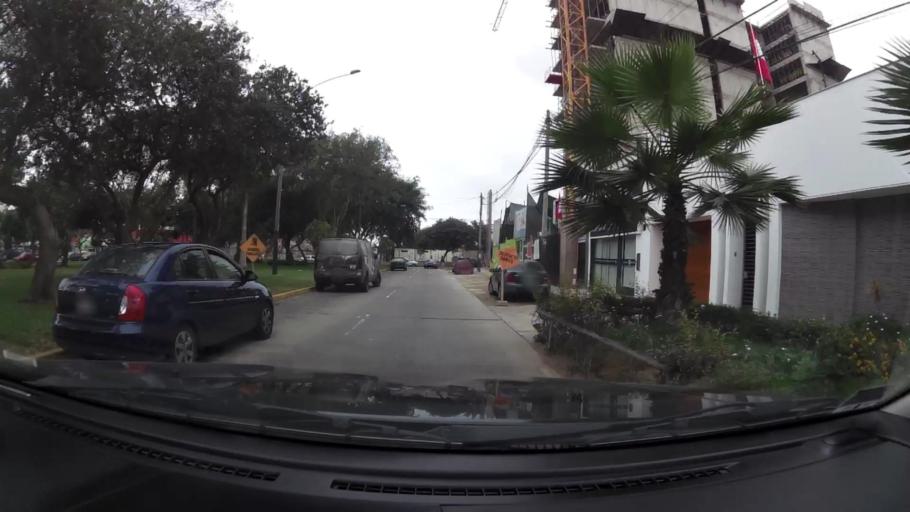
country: PE
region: Lima
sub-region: Lima
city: Surco
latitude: -12.1426
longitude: -77.0016
